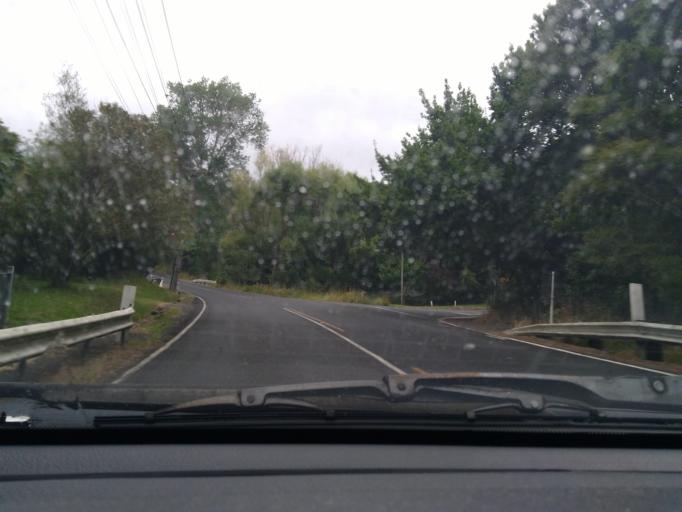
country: NZ
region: Auckland
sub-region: Auckland
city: Waitakere
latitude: -36.9186
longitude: 174.6082
